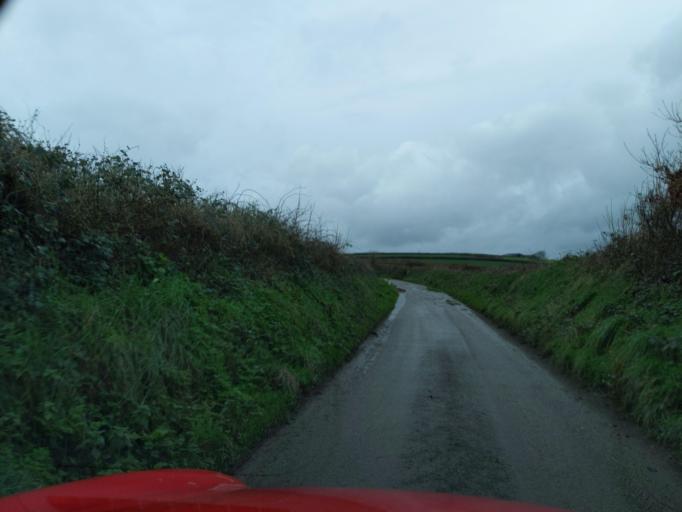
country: GB
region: England
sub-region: Cornwall
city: Duloe
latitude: 50.3477
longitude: -4.5366
